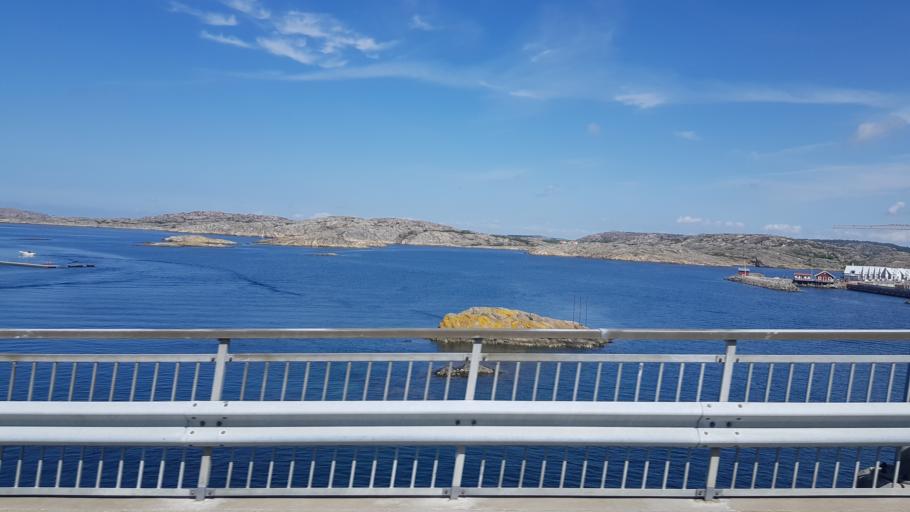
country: SE
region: Vaestra Goetaland
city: Ronnang
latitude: 57.9482
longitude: 11.5524
